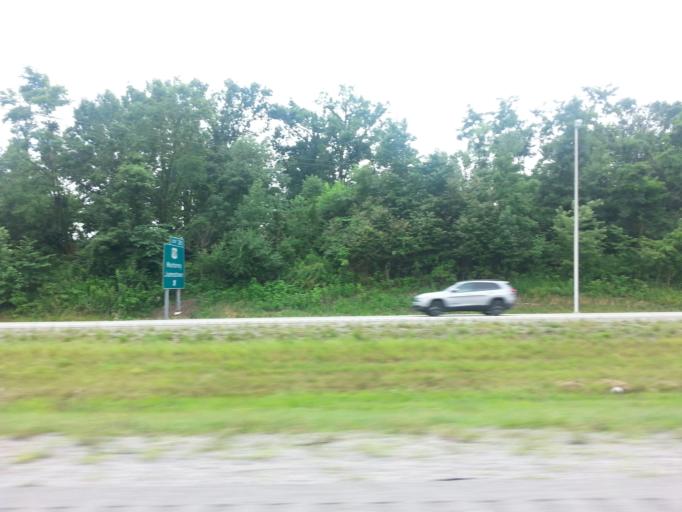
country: US
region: Tennessee
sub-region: Putnam County
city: Monterey
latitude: 36.1402
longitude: -85.2719
